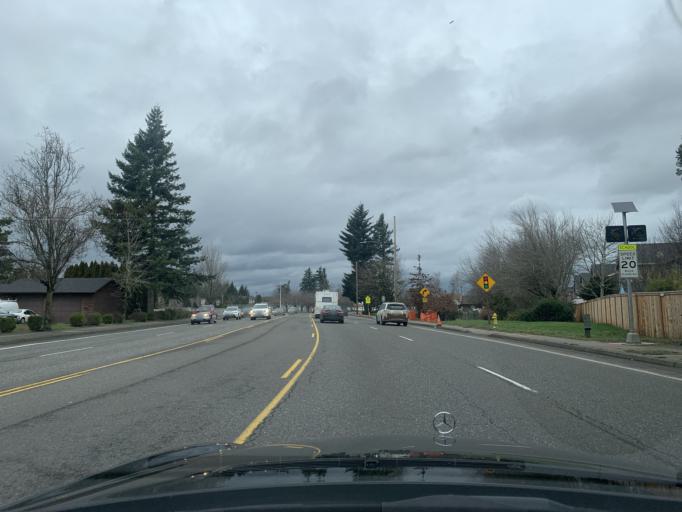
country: US
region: Oregon
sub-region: Multnomah County
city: Troutdale
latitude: 45.5276
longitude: -122.3985
